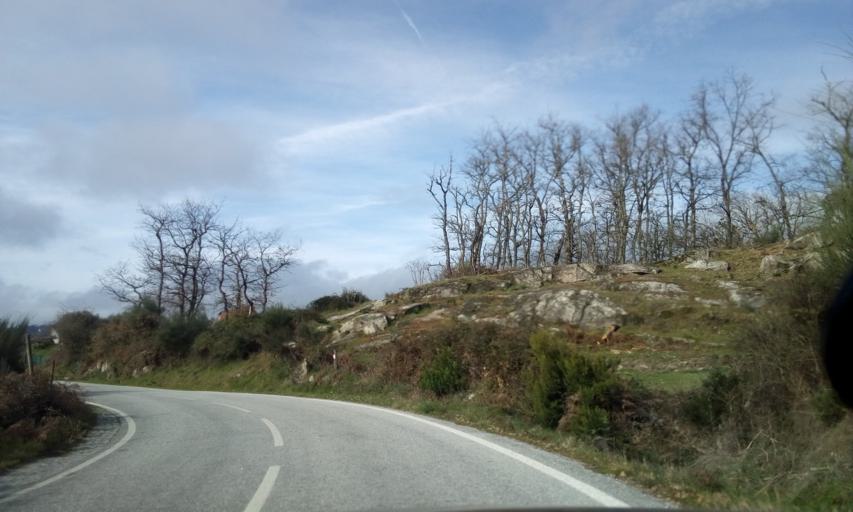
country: PT
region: Guarda
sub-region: Aguiar da Beira
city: Aguiar da Beira
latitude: 40.7474
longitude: -7.5531
